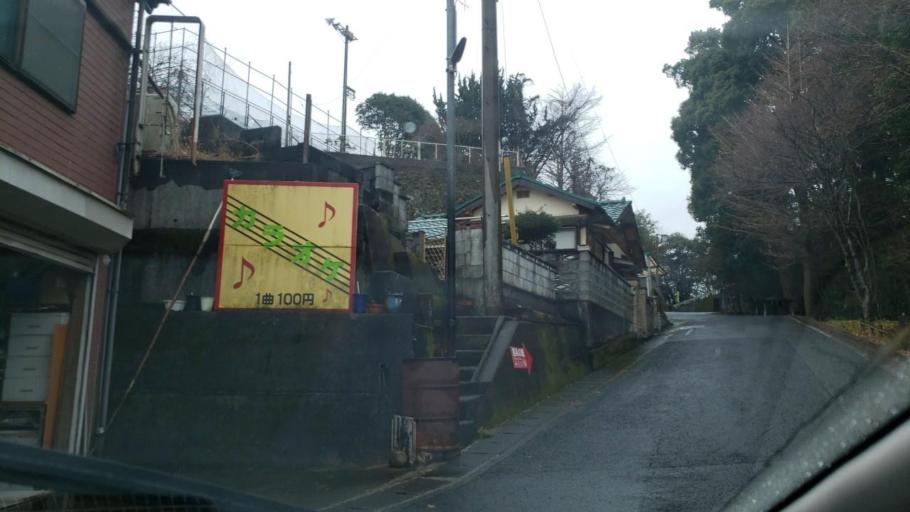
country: JP
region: Tokushima
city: Kamojimacho-jogejima
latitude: 34.0671
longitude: 134.3203
